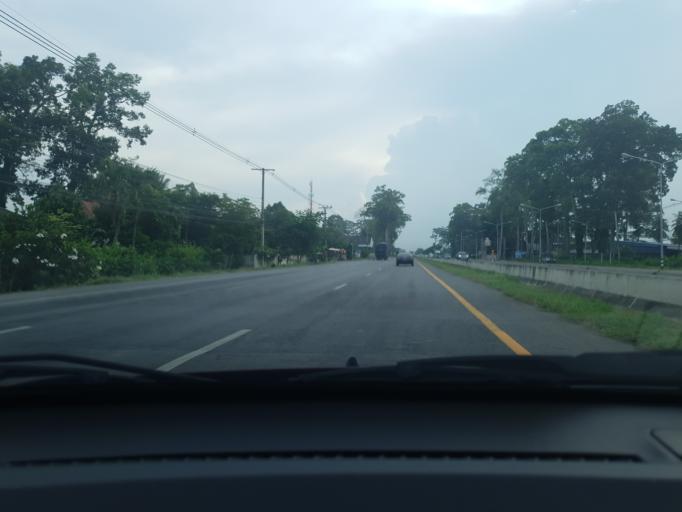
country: TH
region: Phetchaburi
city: Ban Lat
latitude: 13.0149
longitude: 99.9186
